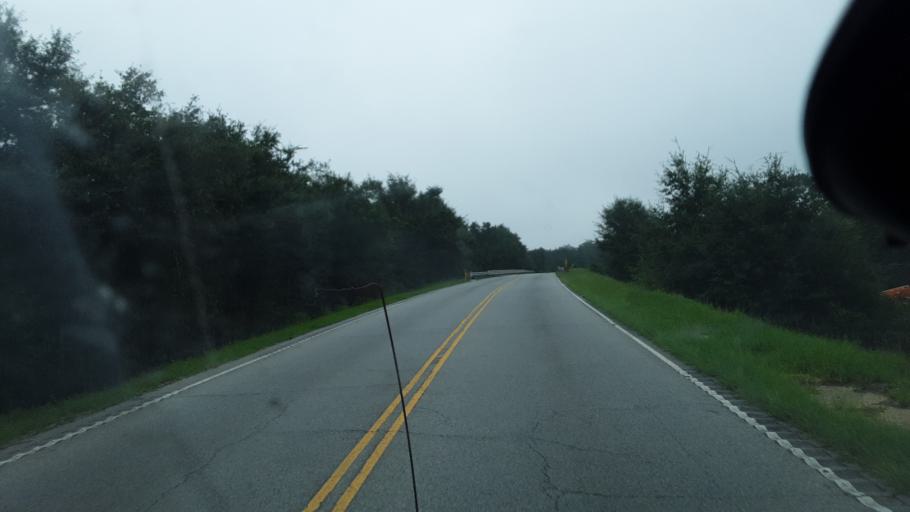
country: US
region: South Carolina
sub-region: Florence County
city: Johnsonville
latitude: 33.9144
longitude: -79.4147
